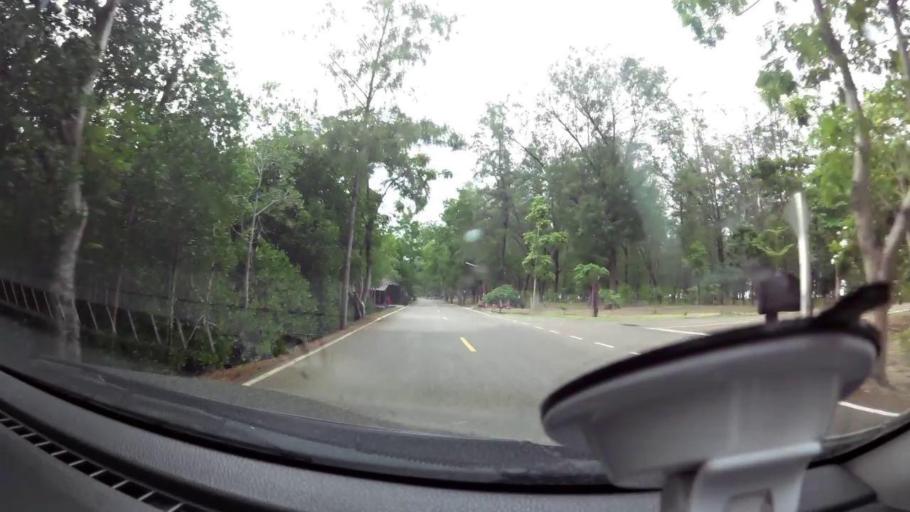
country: TH
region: Prachuap Khiri Khan
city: Pran Buri
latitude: 12.4147
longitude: 99.9850
